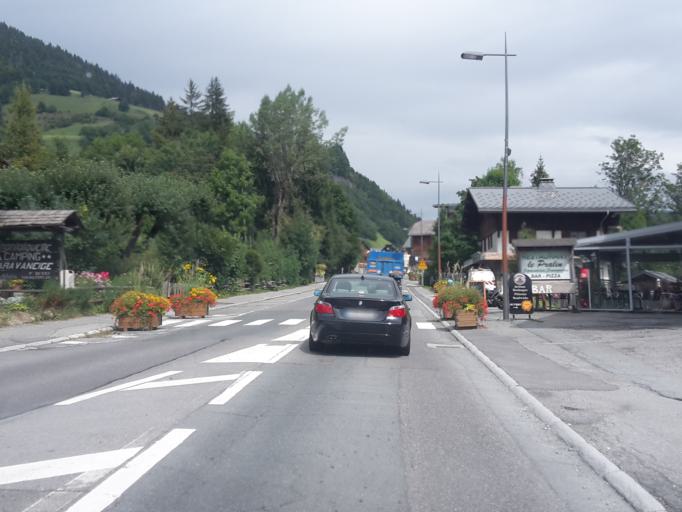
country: FR
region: Rhone-Alpes
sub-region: Departement de la Haute-Savoie
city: Praz-sur-Arly
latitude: 45.8361
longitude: 6.5674
